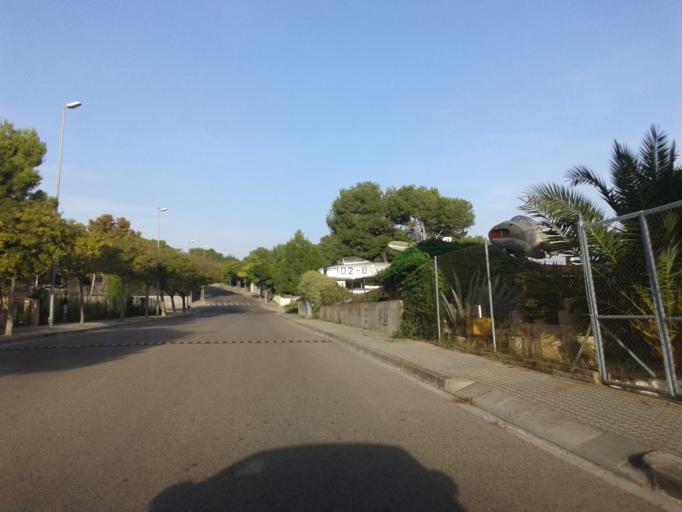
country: ES
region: Catalonia
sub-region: Provincia de Barcelona
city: Vilanova i la Geltru
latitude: 41.2161
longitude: 1.7060
